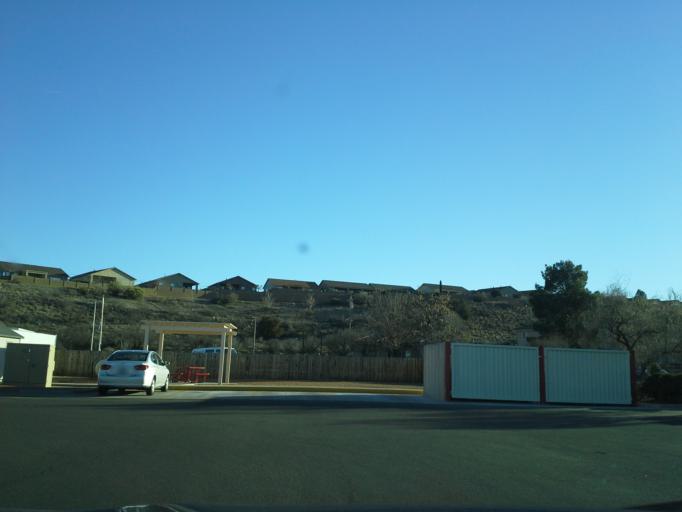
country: US
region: Arizona
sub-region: Yavapai County
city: Camp Verde
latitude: 34.5656
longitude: -111.8638
